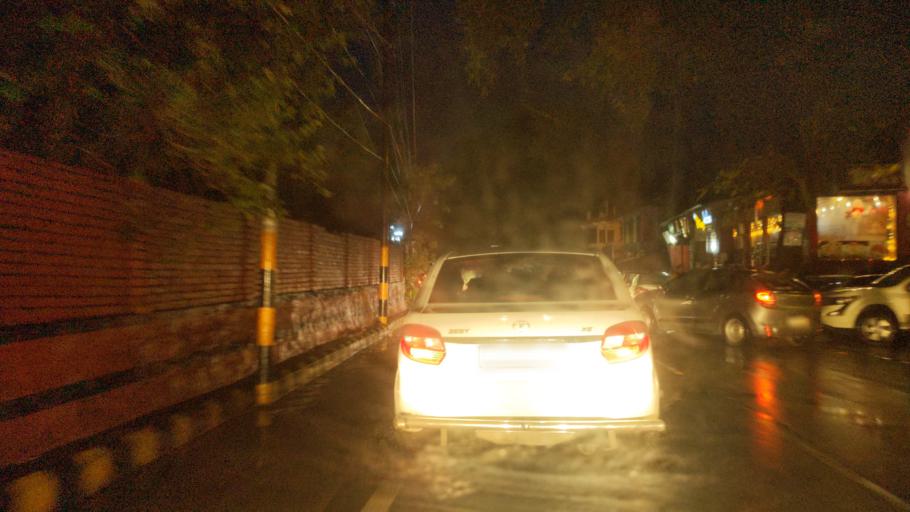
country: IN
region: Uttarakhand
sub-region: Naini Tal
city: Haldwani
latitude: 29.2740
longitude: 79.5451
